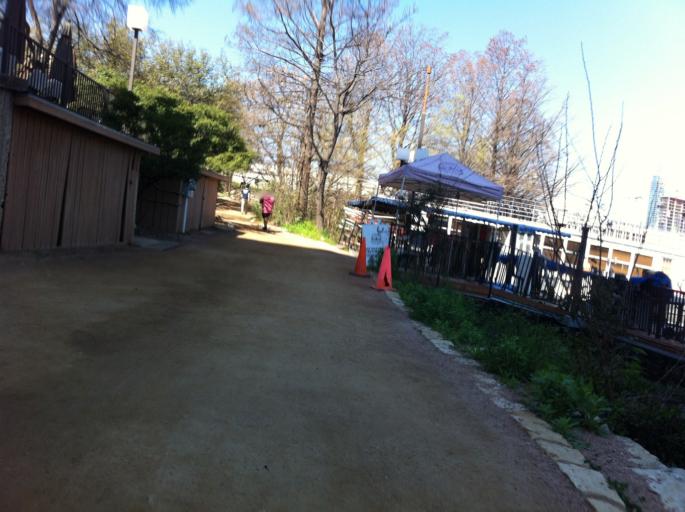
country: US
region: Texas
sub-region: Travis County
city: Austin
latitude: 30.2606
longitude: -97.7453
